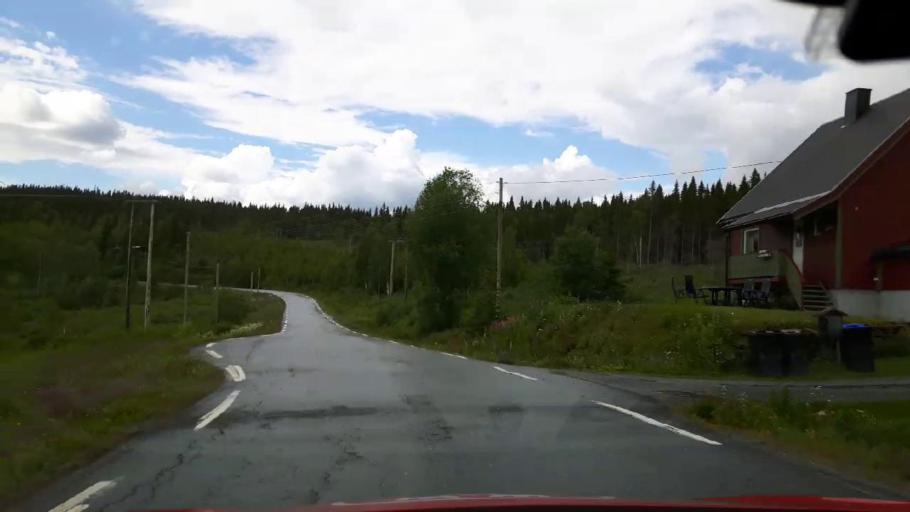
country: NO
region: Nord-Trondelag
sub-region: Lierne
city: Sandvika
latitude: 64.1024
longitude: 14.0227
